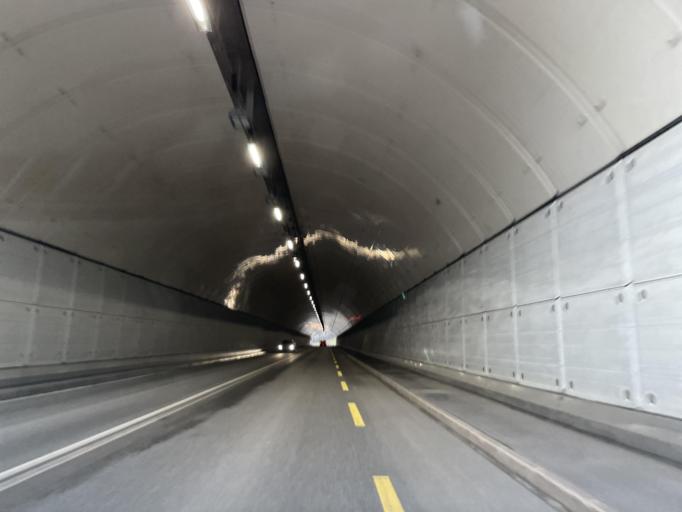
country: CH
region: Saint Gallen
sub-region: Wahlkreis Toggenburg
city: Krummenau
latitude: 47.2368
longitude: 9.1866
